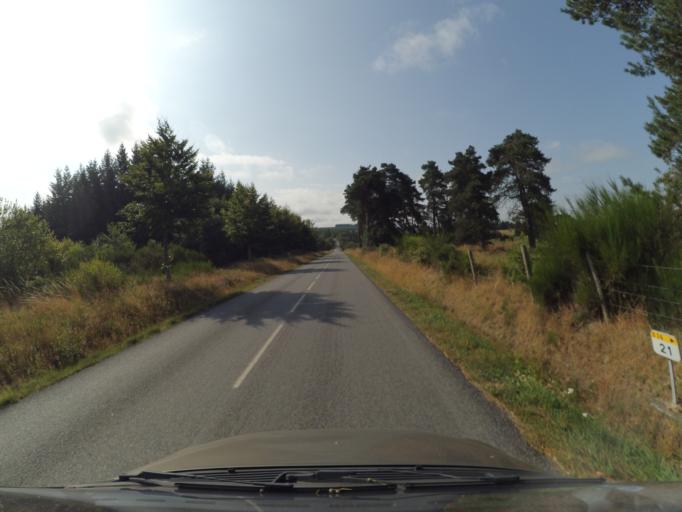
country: FR
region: Limousin
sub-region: Departement de la Correze
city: Meymac
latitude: 45.6262
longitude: 2.1040
